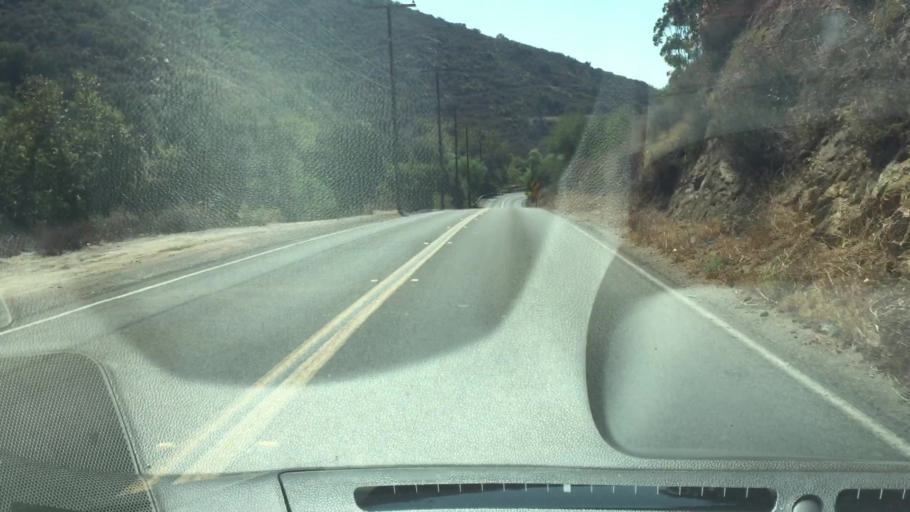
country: US
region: California
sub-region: San Diego County
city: Jamul
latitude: 32.7305
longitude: -116.8755
